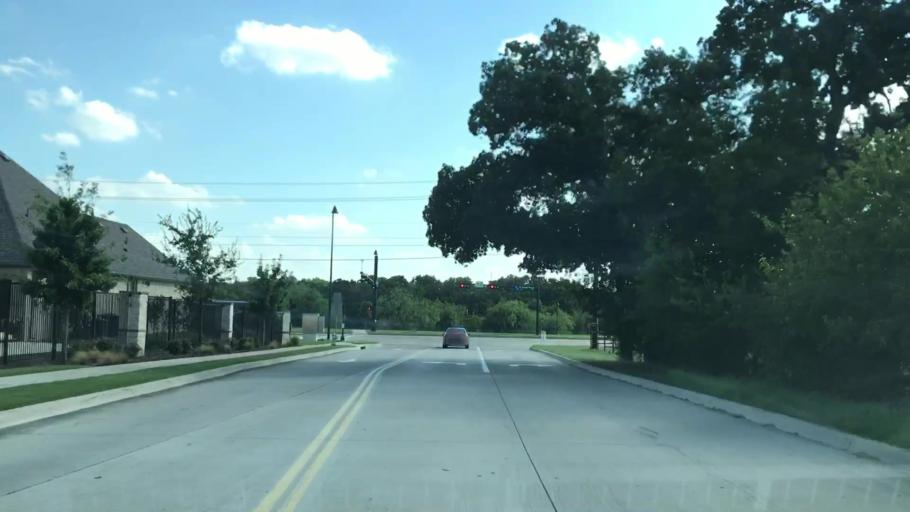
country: US
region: Texas
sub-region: Tarrant County
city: Keller
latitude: 32.9009
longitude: -97.2201
